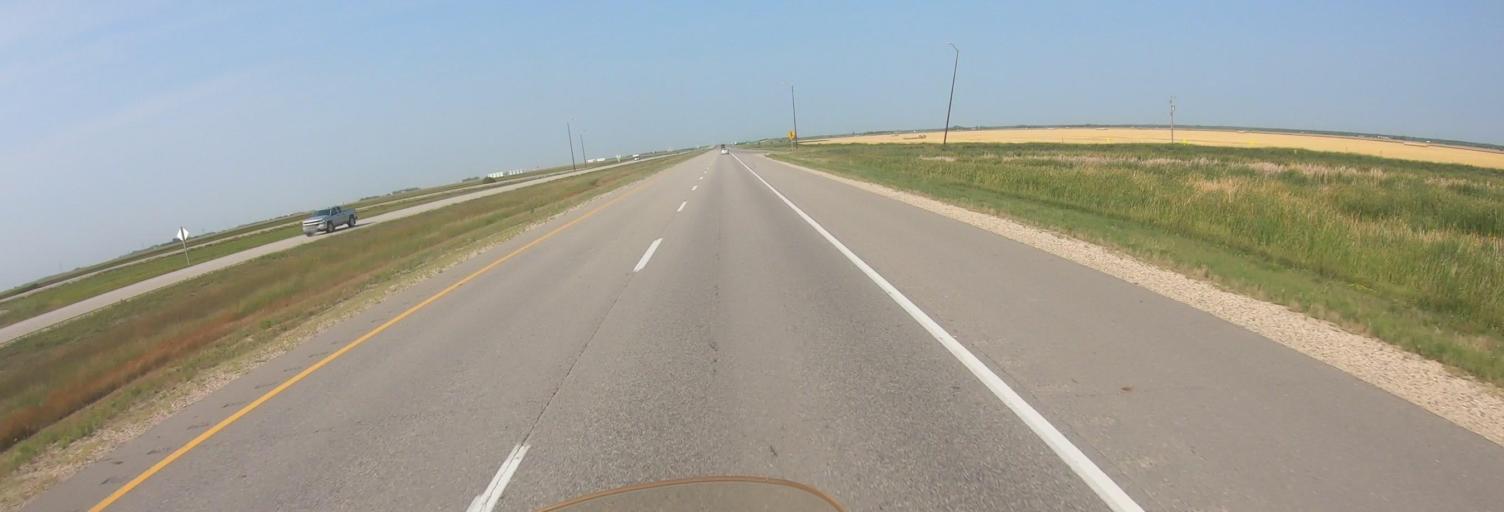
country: CA
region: Manitoba
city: Steinbach
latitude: 49.6812
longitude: -96.6595
